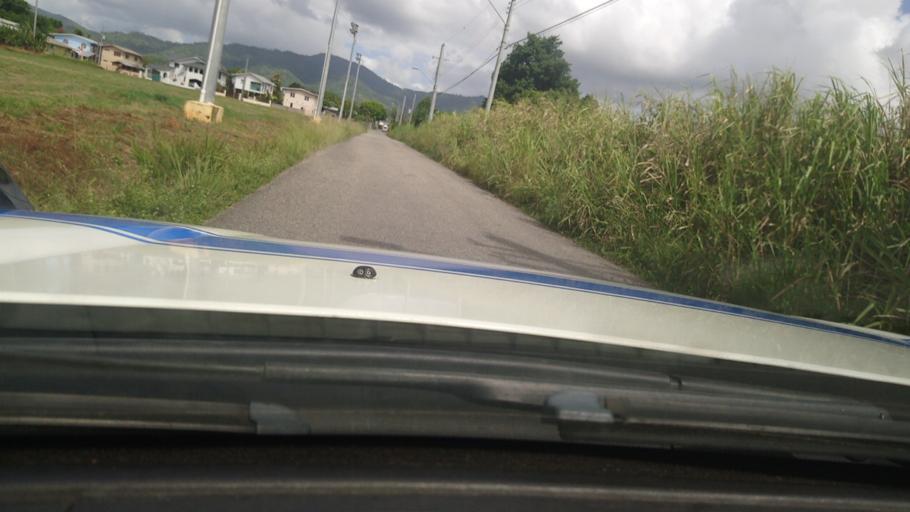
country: TT
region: Borough of Arima
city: Arima
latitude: 10.6220
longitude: -61.3017
